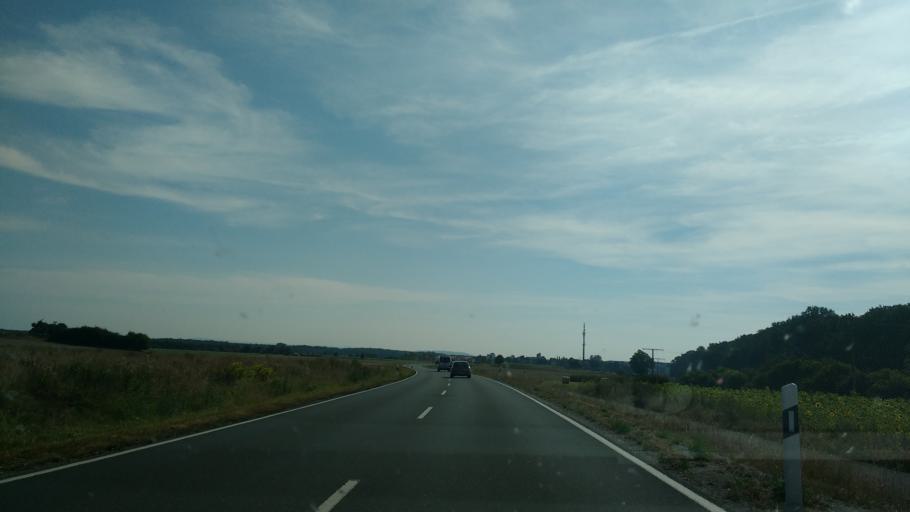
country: DE
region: Bavaria
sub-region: Regierungsbezirk Mittelfranken
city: Grossenseebach
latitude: 49.6314
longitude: 10.8922
